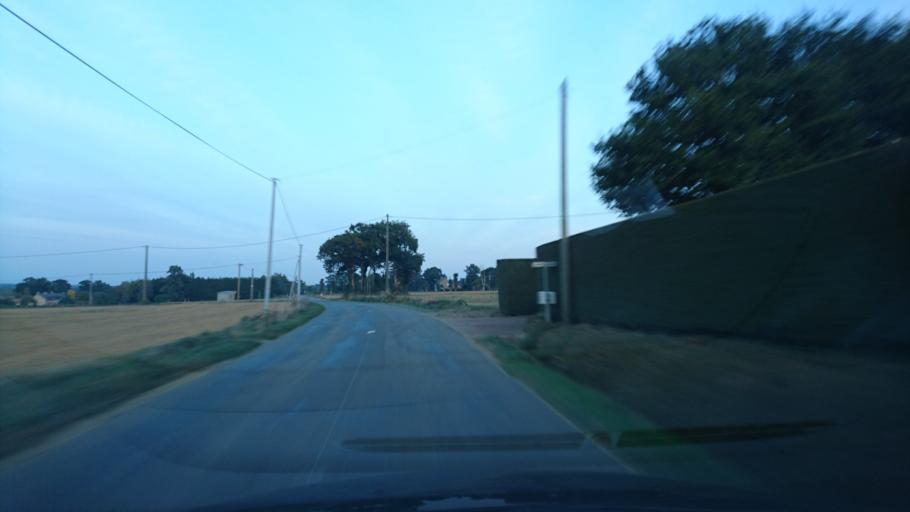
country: FR
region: Brittany
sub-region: Departement d'Ille-et-Vilaine
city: Guignen
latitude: 47.9115
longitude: -1.9018
